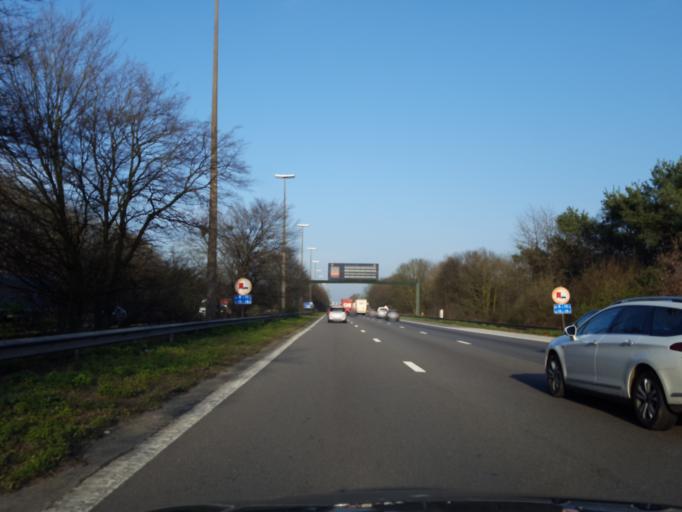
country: BE
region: Wallonia
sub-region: Province du Hainaut
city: Roeulx
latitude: 50.4909
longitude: 4.1036
